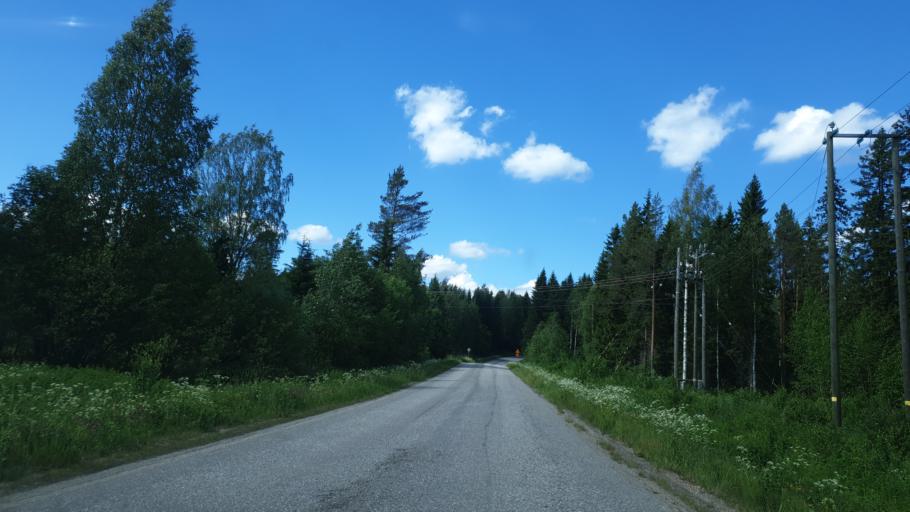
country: FI
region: Northern Savo
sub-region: Koillis-Savo
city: Kaavi
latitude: 63.0209
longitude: 28.6477
